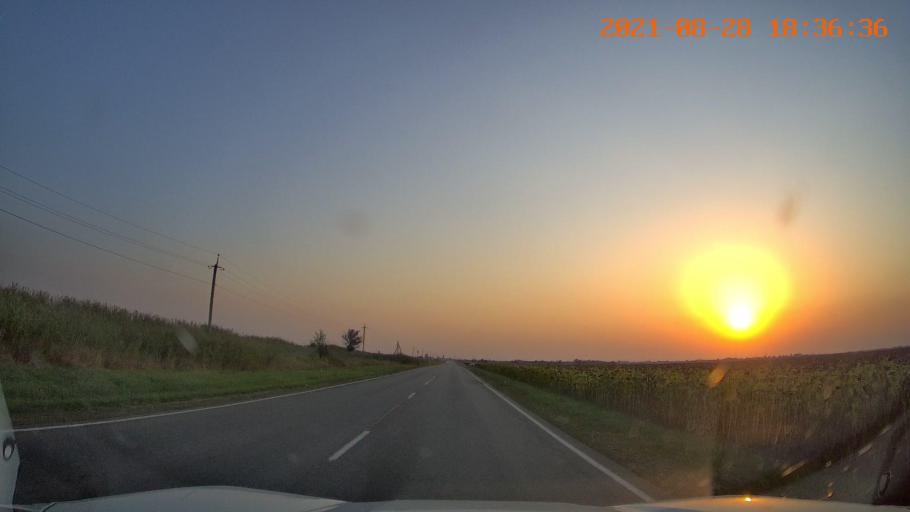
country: RU
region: Adygeya
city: Giaginskaya
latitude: 44.8655
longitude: 40.1081
